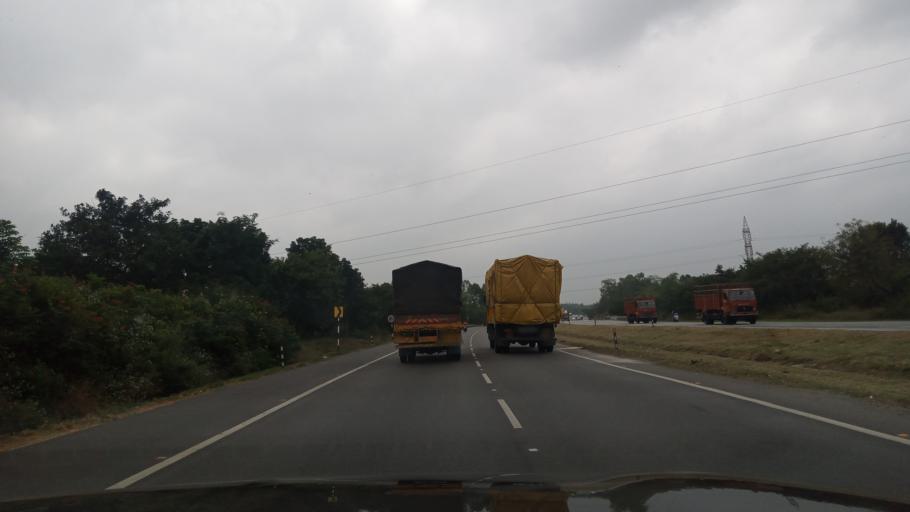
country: IN
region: Karnataka
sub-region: Bangalore Rural
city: Nelamangala
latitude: 13.0374
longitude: 77.4761
